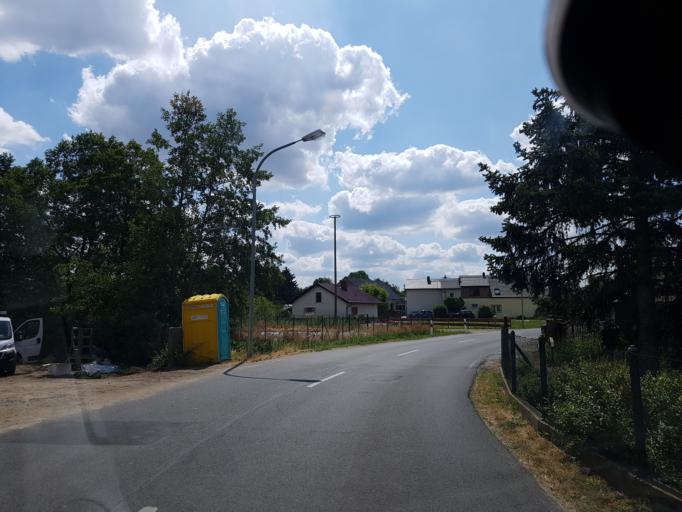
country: DE
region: Brandenburg
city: Drebkau
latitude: 51.6854
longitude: 14.2741
